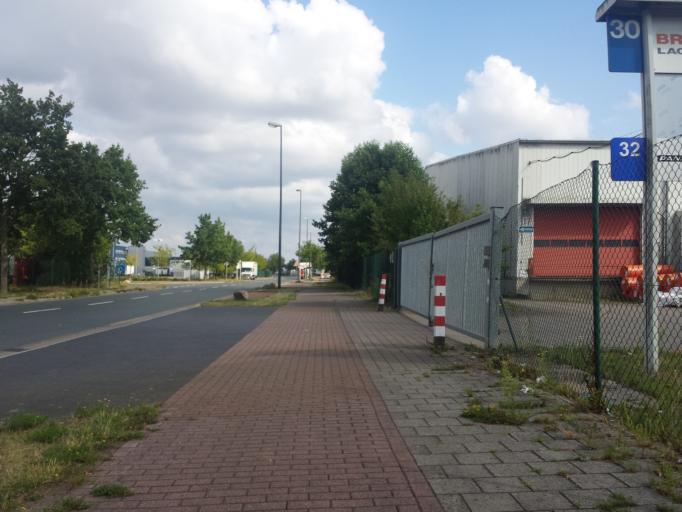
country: DE
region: Lower Saxony
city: Stuhr
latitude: 53.0908
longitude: 8.7028
